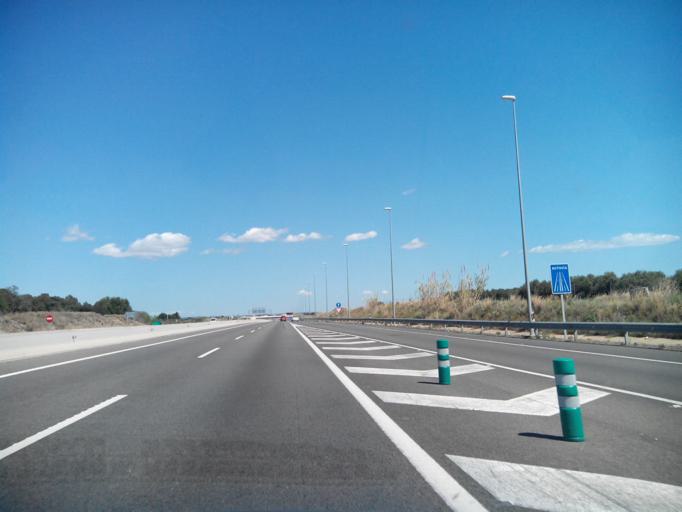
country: ES
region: Catalonia
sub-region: Provincia de Tarragona
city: Salou
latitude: 41.0923
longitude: 1.1006
